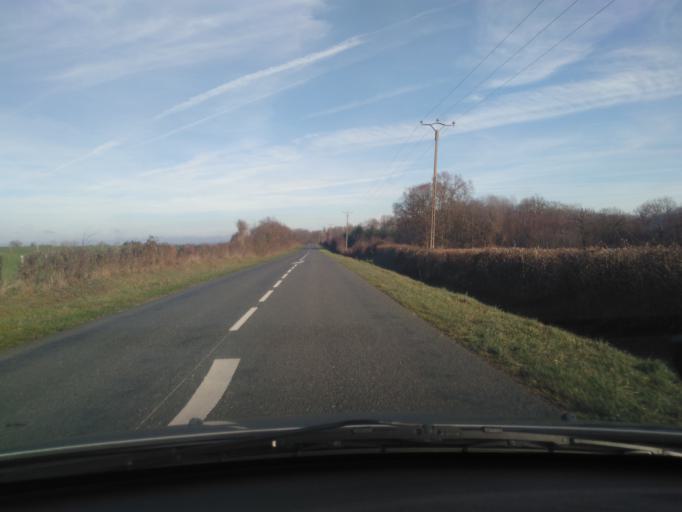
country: FR
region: Centre
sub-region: Departement du Cher
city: Orval
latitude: 46.6663
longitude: 2.4504
